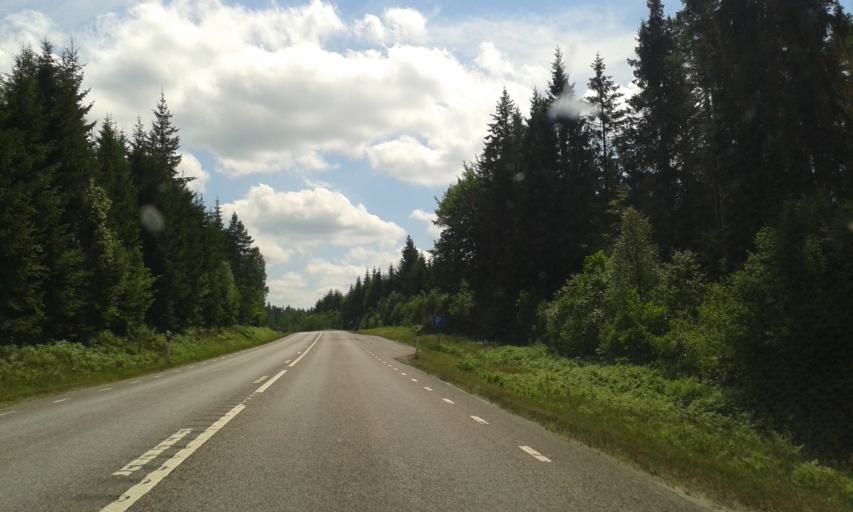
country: SE
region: Joenkoeping
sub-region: Varnamo Kommun
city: Rydaholm
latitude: 56.9438
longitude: 14.3626
